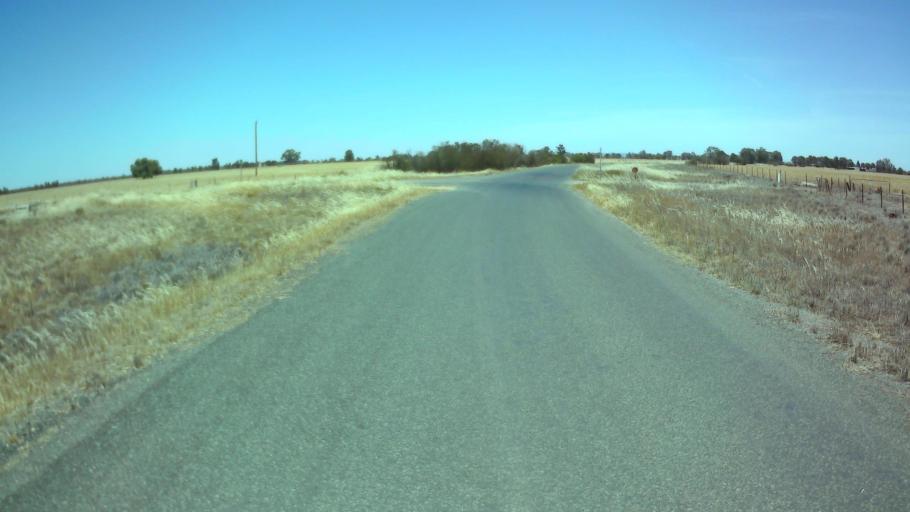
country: AU
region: New South Wales
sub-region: Weddin
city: Grenfell
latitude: -34.0398
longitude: 147.7895
